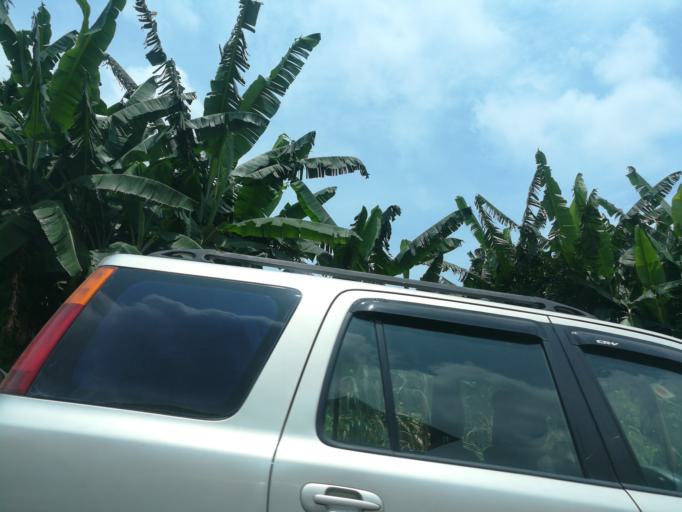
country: NG
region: Lagos
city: Ikeja
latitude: 6.5944
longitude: 3.3606
